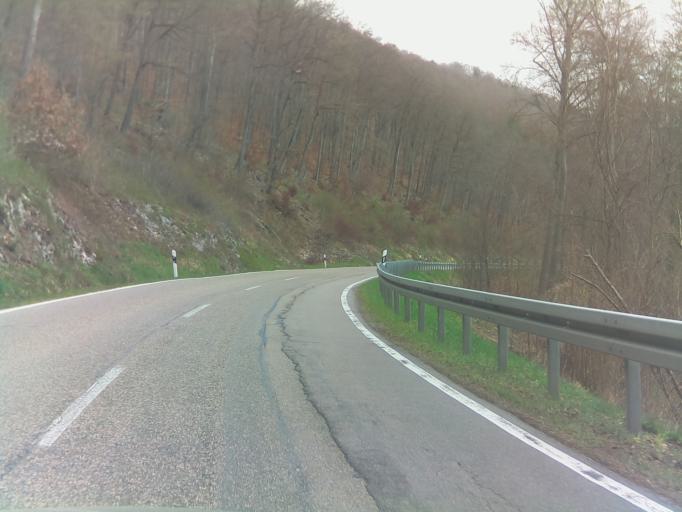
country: DE
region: Baden-Wuerttemberg
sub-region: Tuebingen Region
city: Schelklingen
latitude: 48.3847
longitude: 9.7211
